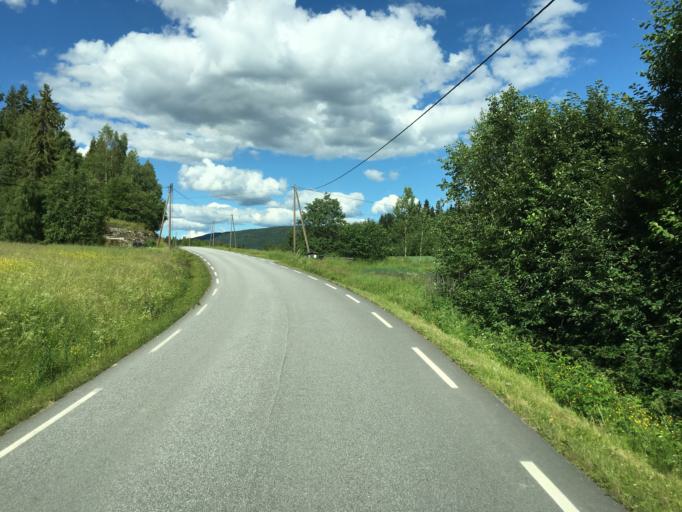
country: NO
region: Oppland
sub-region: Sondre Land
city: Hov
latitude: 60.6192
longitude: 10.3396
